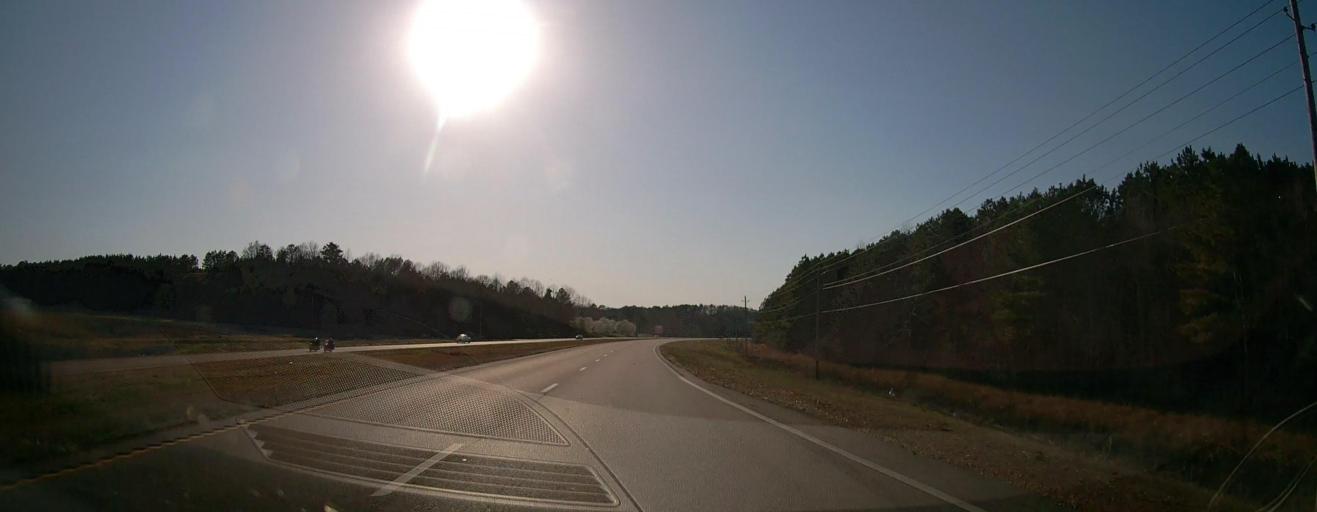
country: US
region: Mississippi
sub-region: Alcorn County
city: Farmington
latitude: 34.8570
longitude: -88.3830
